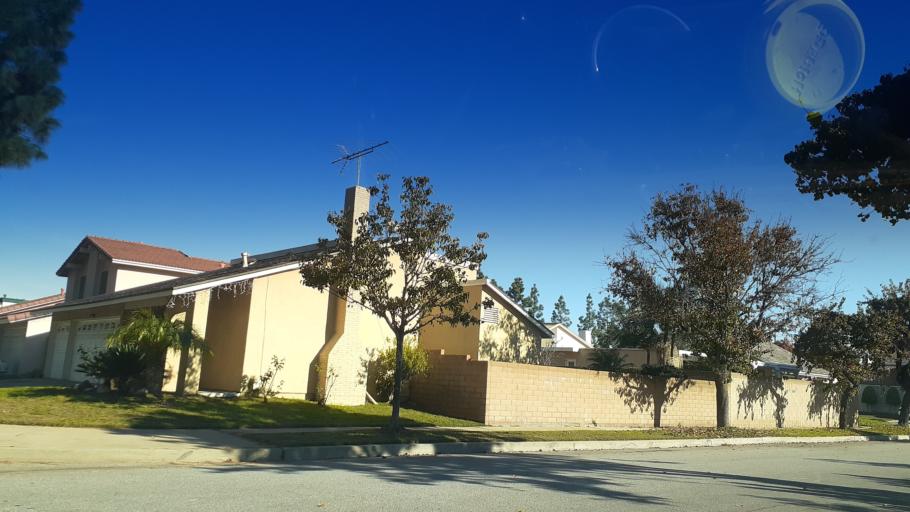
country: US
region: California
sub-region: Los Angeles County
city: Cerritos
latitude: 33.8560
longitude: -118.0662
